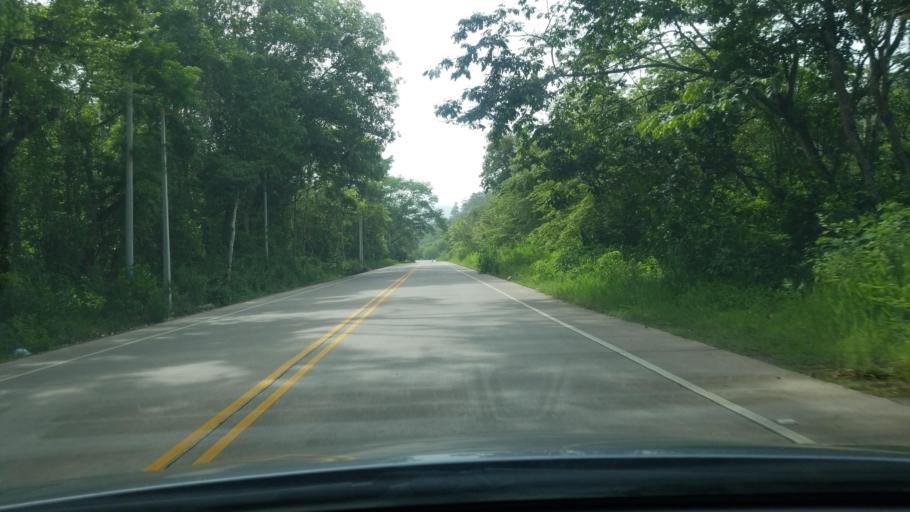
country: HN
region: Copan
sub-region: Santa Rita
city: Santa Rita, Copan
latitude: 14.8707
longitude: -89.0765
